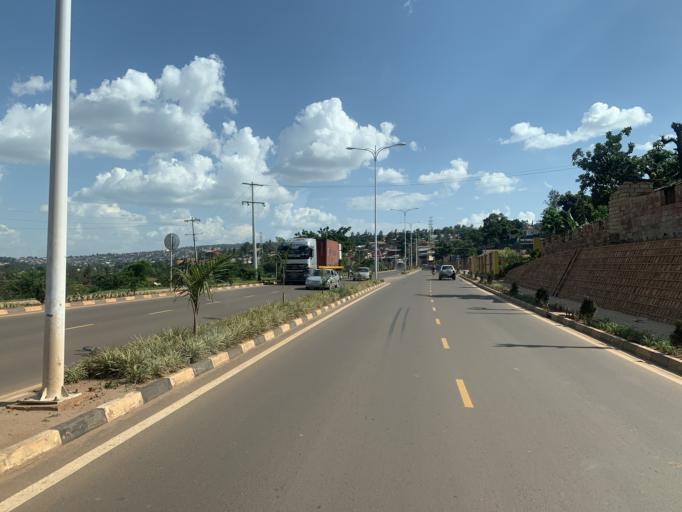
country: RW
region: Kigali
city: Kigali
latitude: -1.9599
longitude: 30.0770
